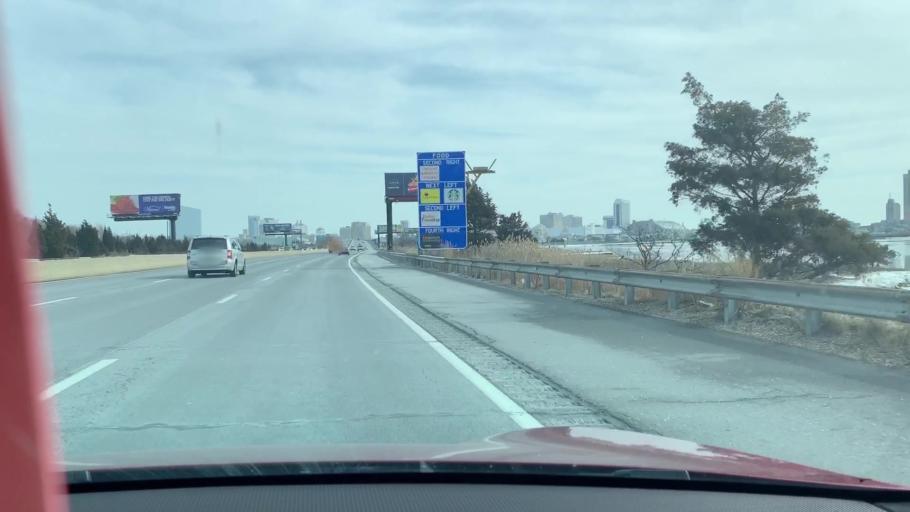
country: US
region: New Jersey
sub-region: Atlantic County
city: Atlantic City
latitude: 39.3667
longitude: -74.4563
